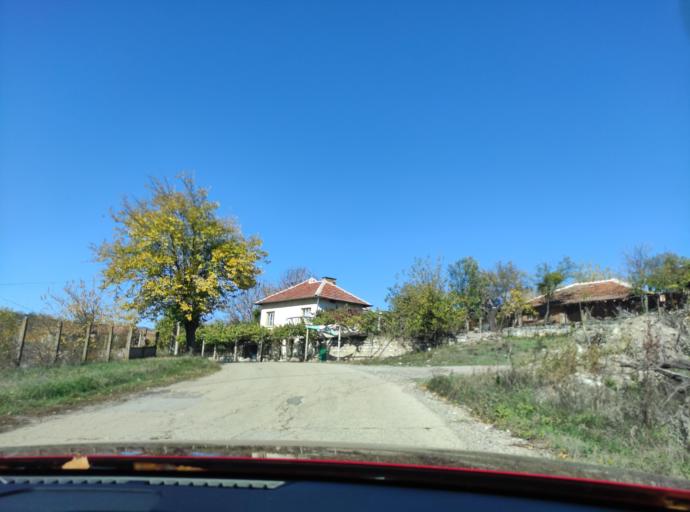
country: BG
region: Montana
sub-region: Obshtina Montana
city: Montana
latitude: 43.4340
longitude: 23.0599
